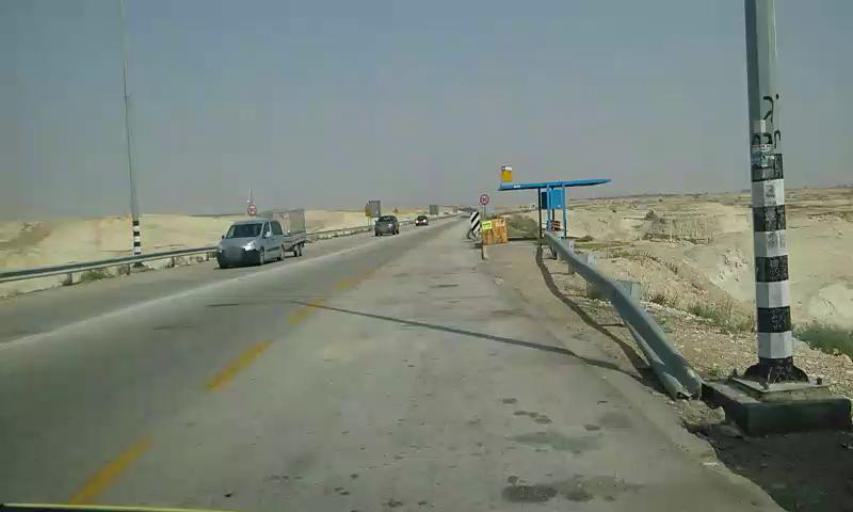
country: PS
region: West Bank
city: Jericho
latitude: 31.8002
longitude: 35.4908
